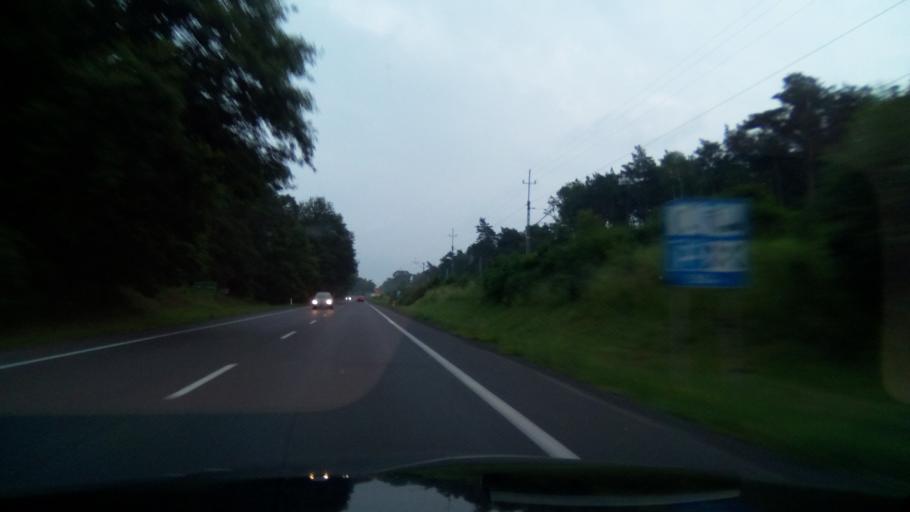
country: PL
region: Greater Poland Voivodeship
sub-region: Powiat poznanski
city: Kostrzyn
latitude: 52.4709
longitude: 17.2049
